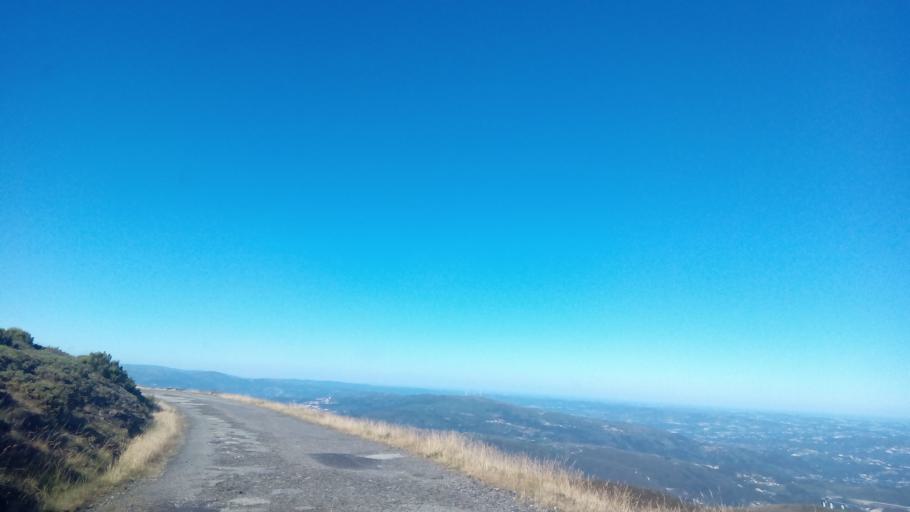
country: PT
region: Vila Real
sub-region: Mesao Frio
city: Mesao Frio
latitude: 41.2565
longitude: -7.8984
